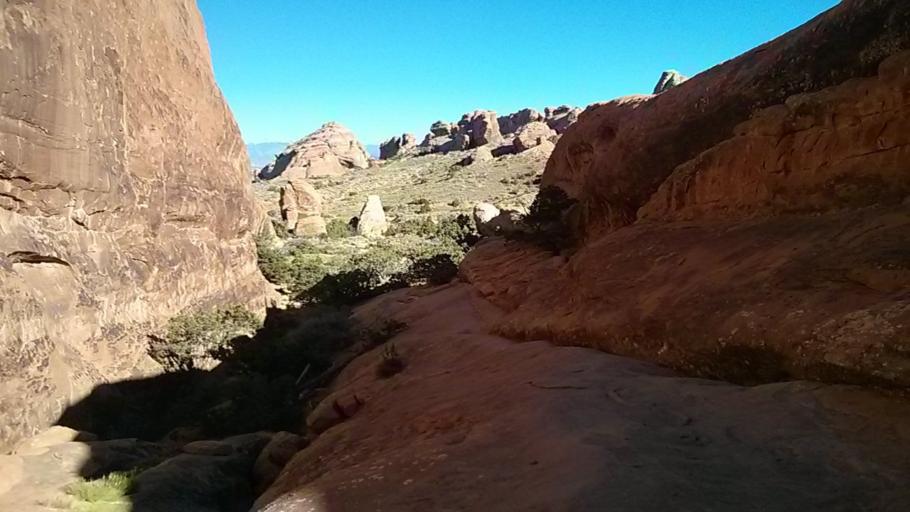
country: US
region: Utah
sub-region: Grand County
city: Moab
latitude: 38.7923
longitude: -109.6074
